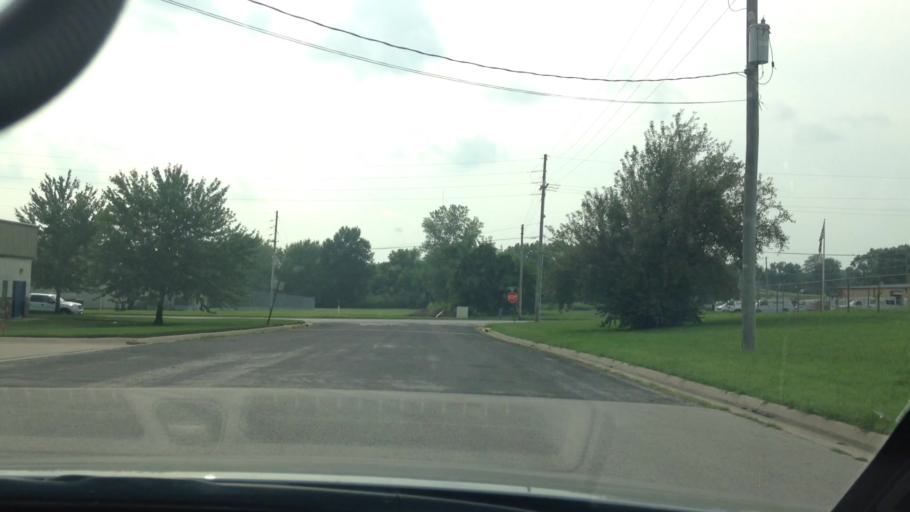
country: US
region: Kansas
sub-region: Leavenworth County
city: Lansing
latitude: 39.2732
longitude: -94.8935
